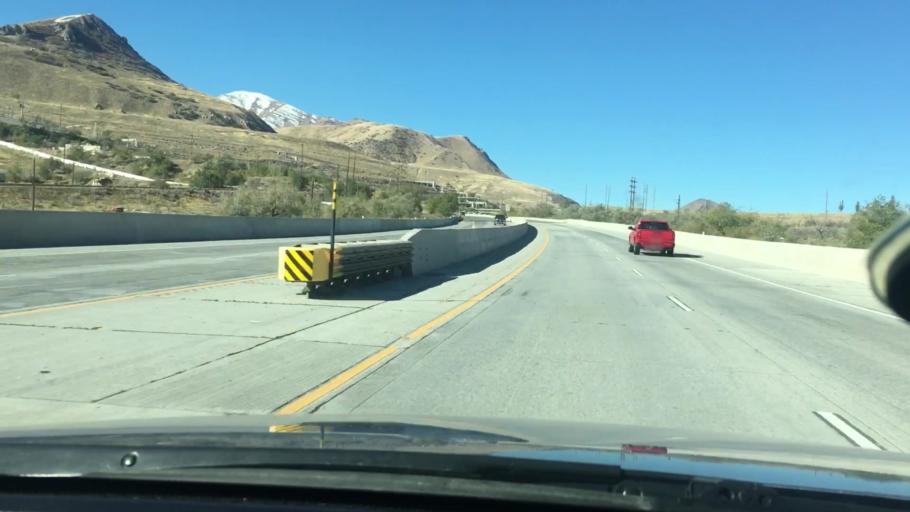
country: US
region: Utah
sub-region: Salt Lake County
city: Magna
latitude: 40.7178
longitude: -112.1160
